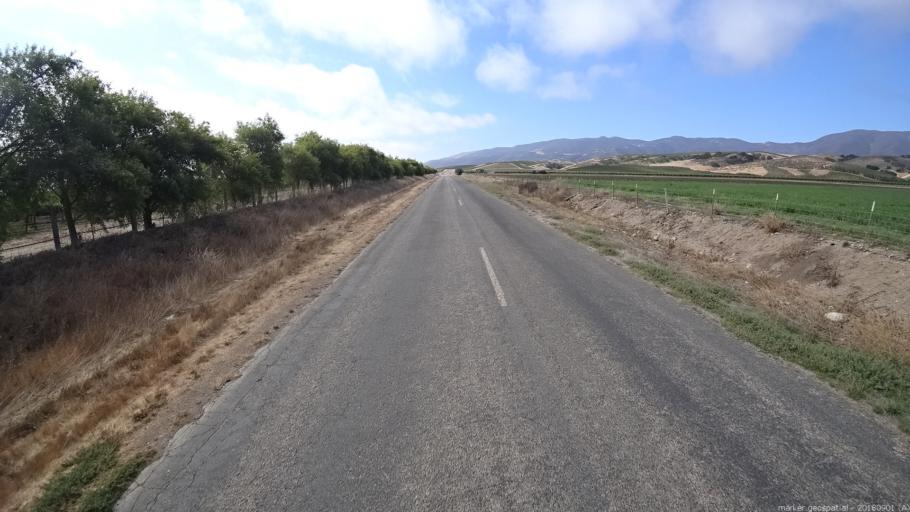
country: US
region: California
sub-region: Monterey County
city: Soledad
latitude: 36.3615
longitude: -121.3355
